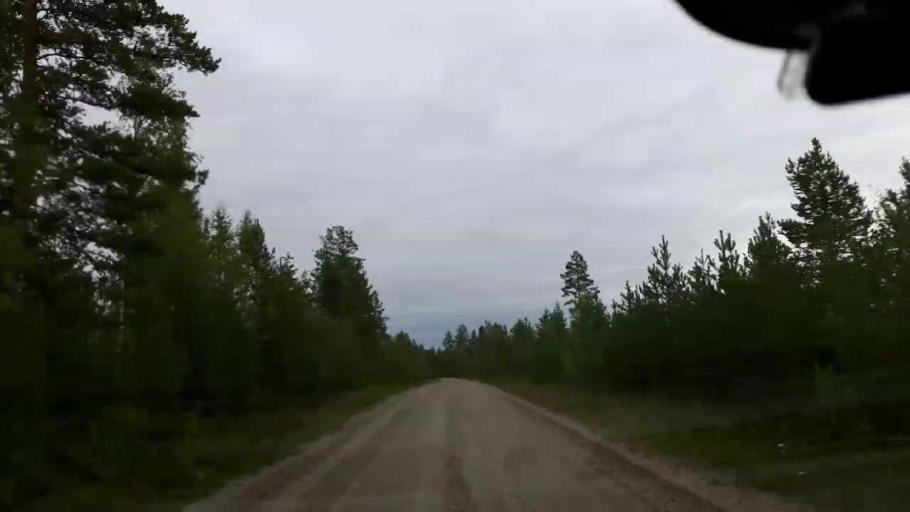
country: SE
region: Vaesternorrland
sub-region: Ange Kommun
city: Ange
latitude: 62.8130
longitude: 15.7211
